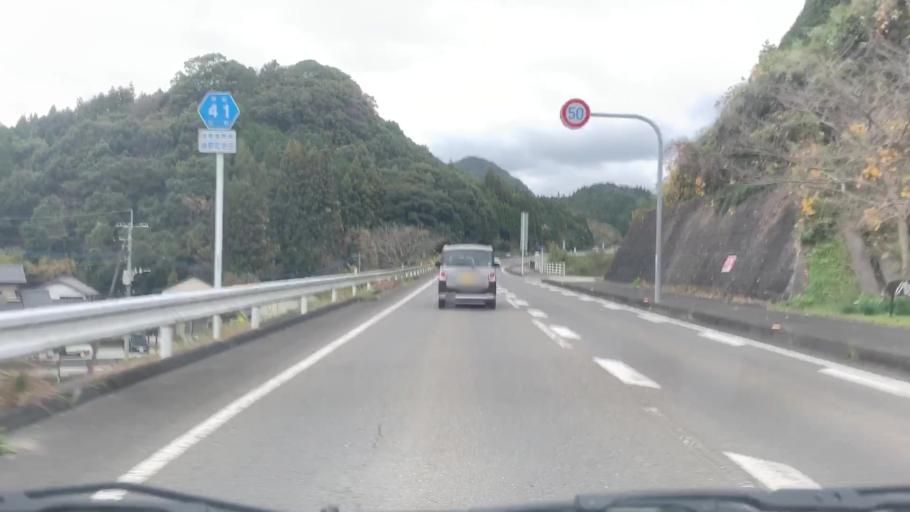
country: JP
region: Saga Prefecture
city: Ureshinomachi-shimojuku
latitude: 33.0929
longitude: 130.0281
